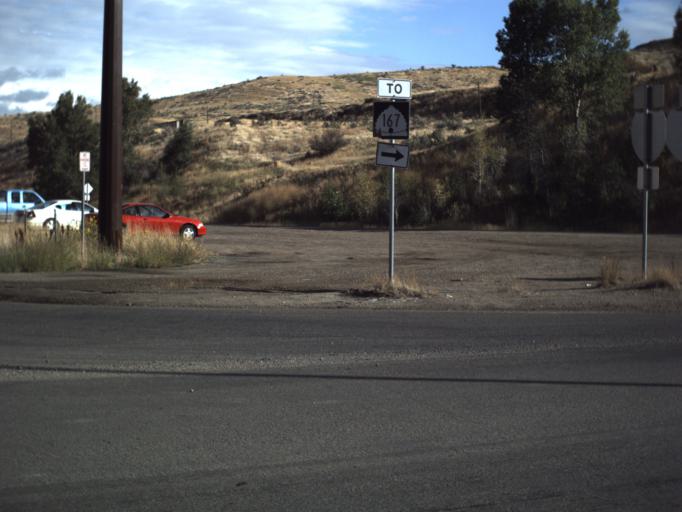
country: US
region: Utah
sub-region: Morgan County
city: Mountain Green
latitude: 41.1157
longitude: -111.7630
